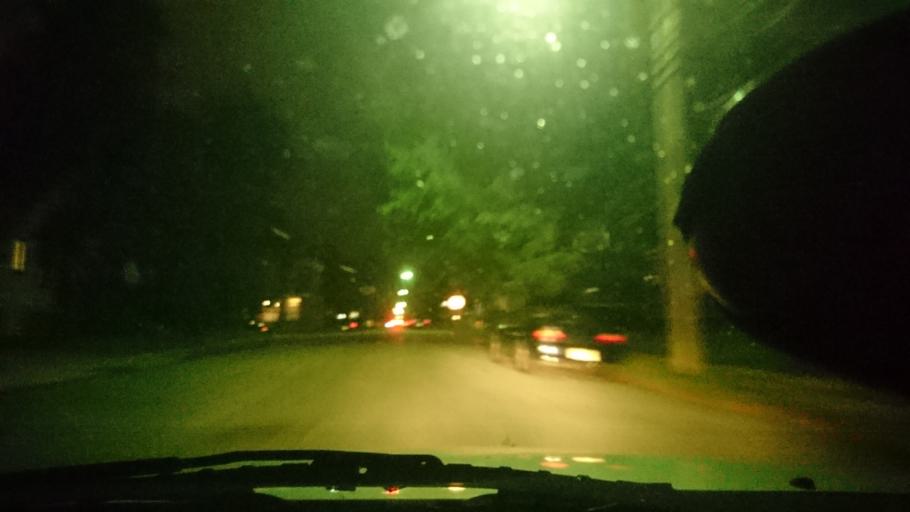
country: US
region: Pennsylvania
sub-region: Delaware County
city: Chester
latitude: 39.8644
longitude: -75.3589
